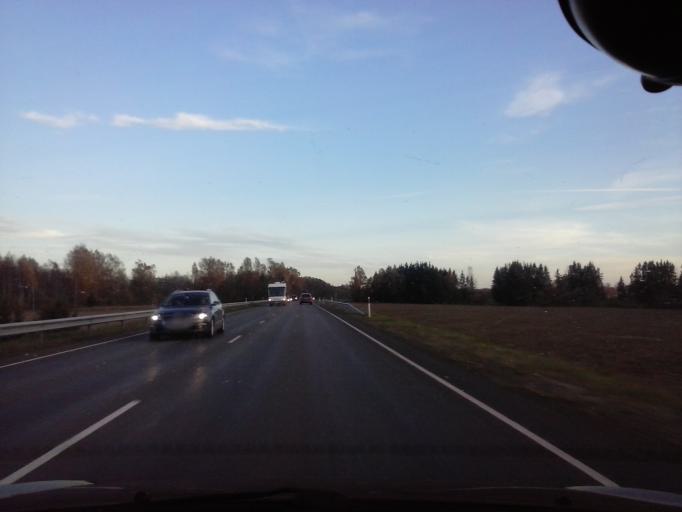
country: EE
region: Harju
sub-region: Nissi vald
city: Turba
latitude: 58.9287
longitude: 24.1050
